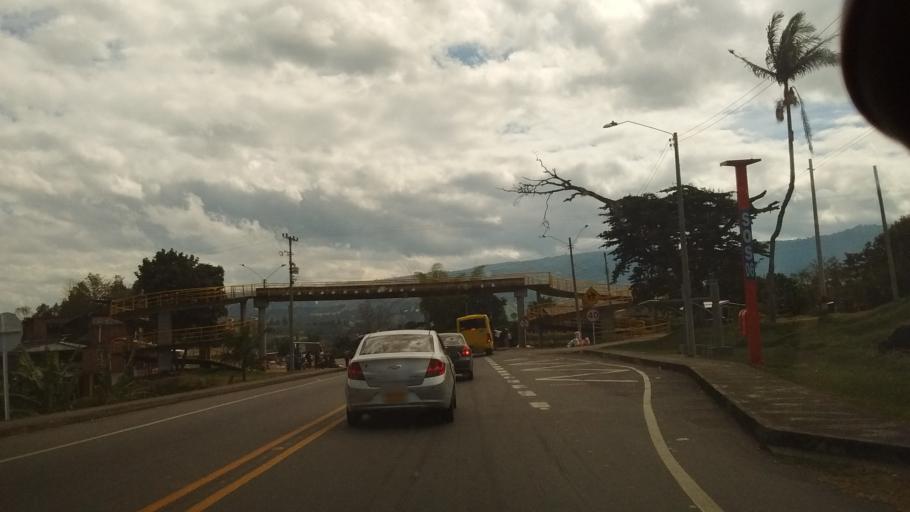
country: CO
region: Cauca
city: Cajibio
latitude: 2.5977
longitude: -76.5269
